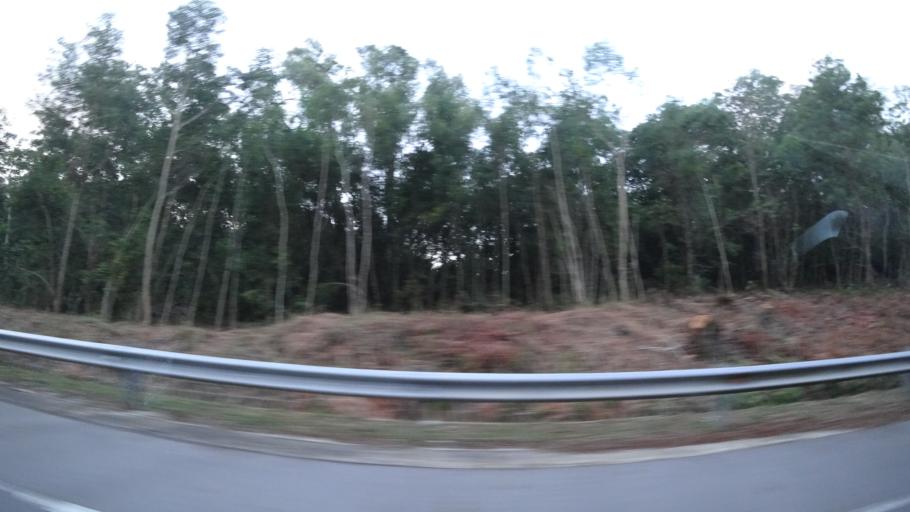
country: BN
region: Brunei and Muara
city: Bandar Seri Begawan
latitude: 4.9353
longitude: 114.8262
